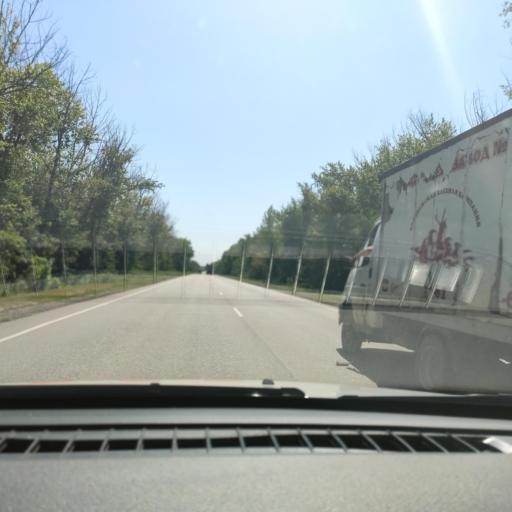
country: RU
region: Voronezj
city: Ostrogozhsk
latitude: 51.0143
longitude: 38.9888
